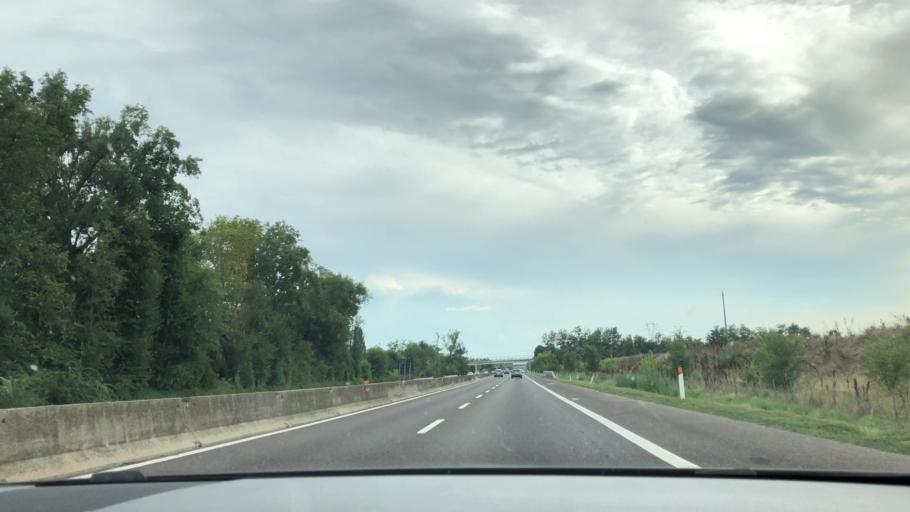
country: IT
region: Emilia-Romagna
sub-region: Provincia di Bologna
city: Bentivoglio
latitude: 44.6140
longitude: 11.4144
